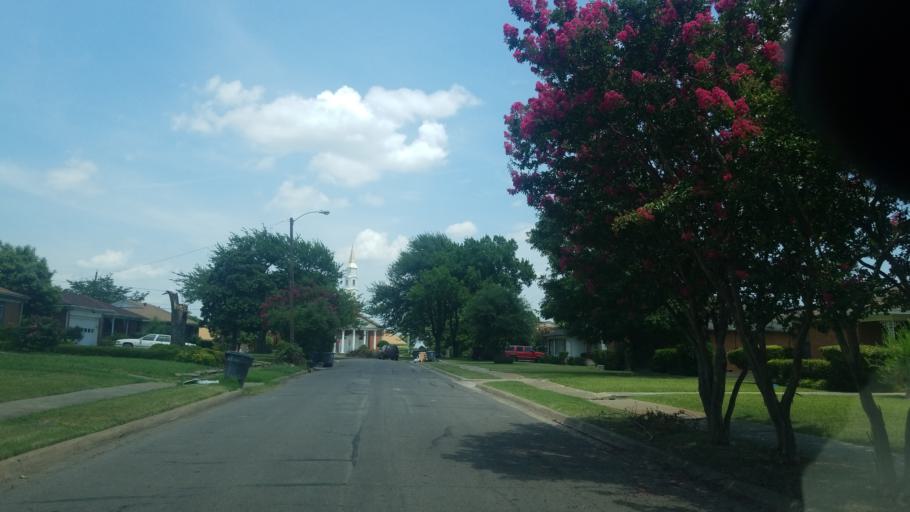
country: US
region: Texas
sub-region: Dallas County
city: Dallas
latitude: 32.7194
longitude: -96.7817
